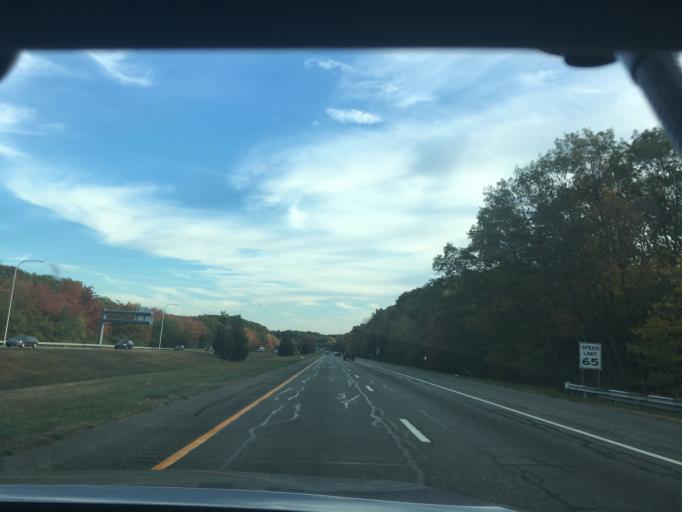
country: US
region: Rhode Island
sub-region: Providence County
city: Johnston
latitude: 41.7856
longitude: -71.5047
